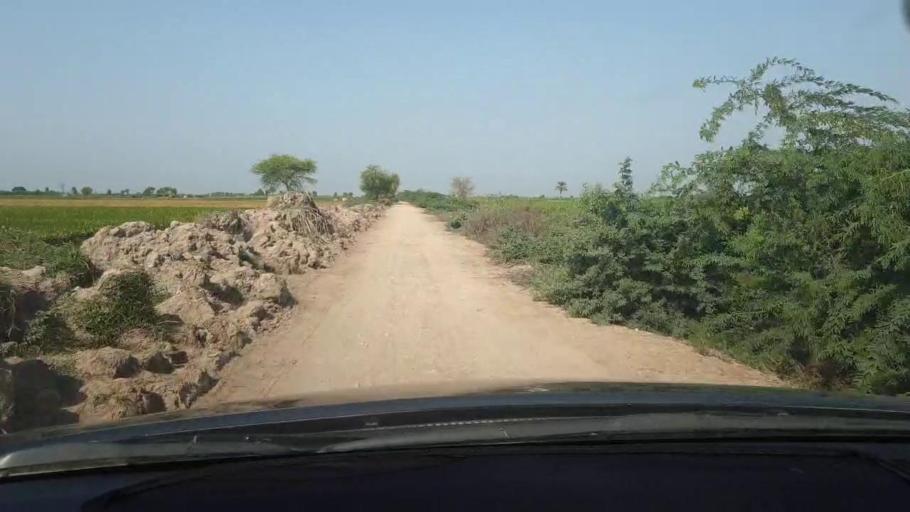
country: PK
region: Sindh
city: Tando Bago
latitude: 24.6800
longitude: 69.1448
